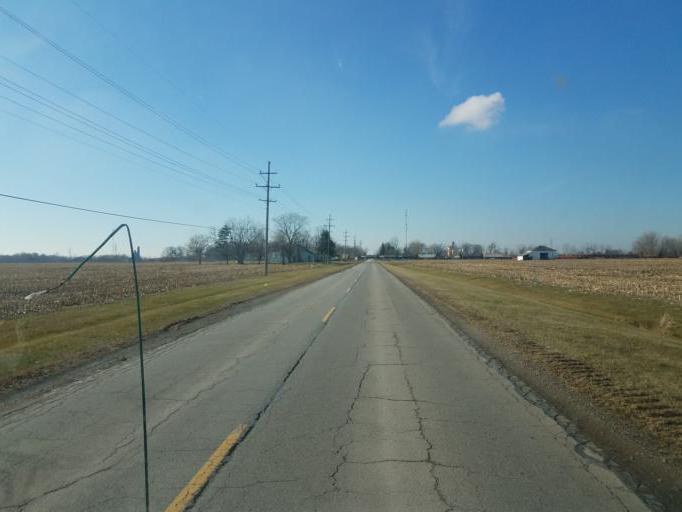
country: US
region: Ohio
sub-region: Marion County
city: Marion
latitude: 40.6294
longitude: -83.1133
